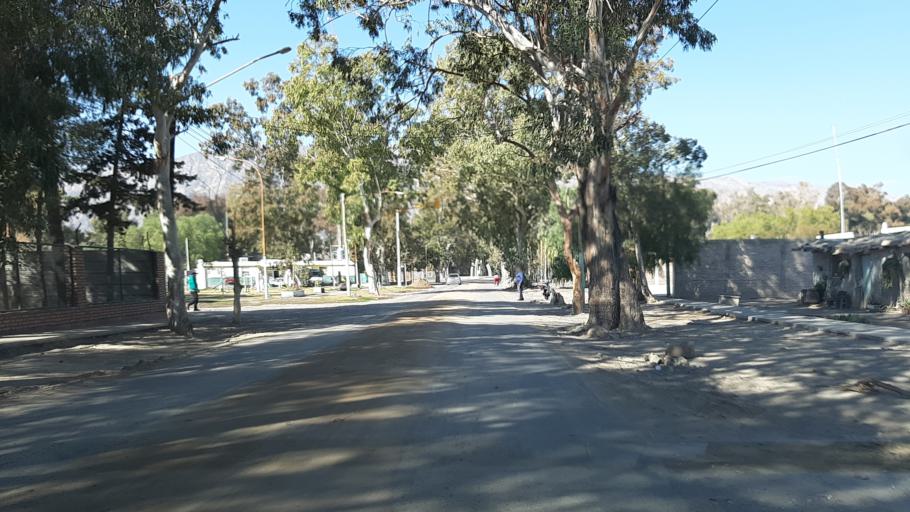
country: AR
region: San Juan
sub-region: Departamento de Zonda
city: Zonda
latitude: -31.5523
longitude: -68.7302
